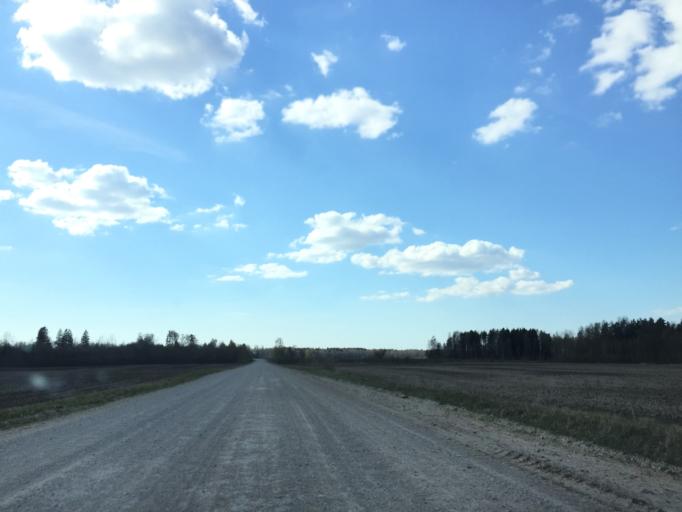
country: LV
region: Krimulda
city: Ragana
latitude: 57.3381
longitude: 24.6338
